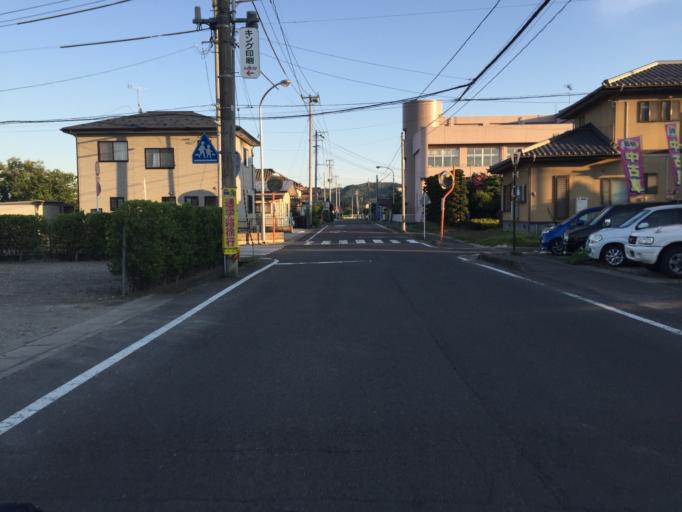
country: JP
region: Fukushima
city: Fukushima-shi
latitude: 37.7354
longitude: 140.4182
